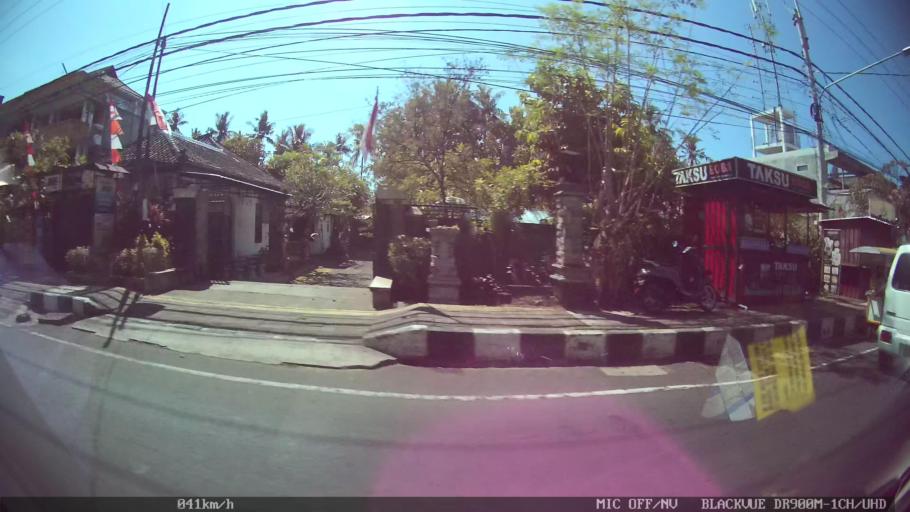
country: ID
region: Bali
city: Banjar Bunutpanggang
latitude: -8.1617
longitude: 115.0273
